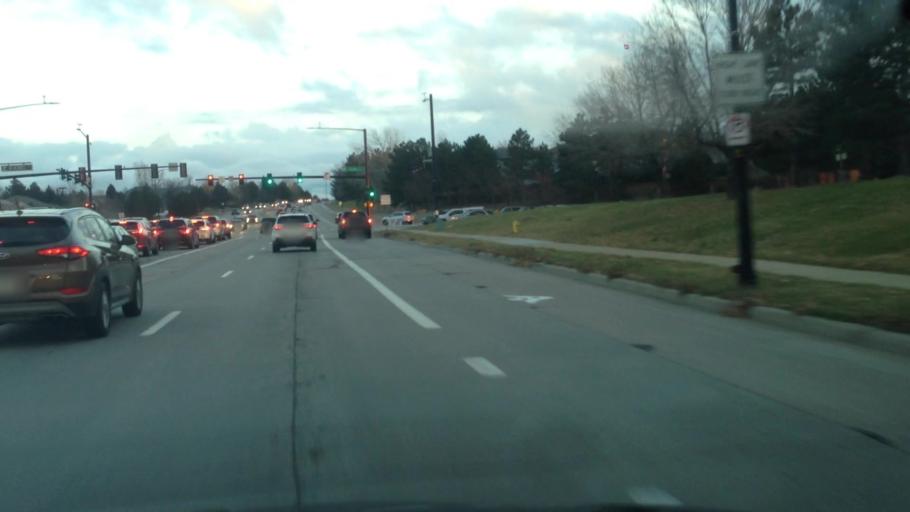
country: US
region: Colorado
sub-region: Douglas County
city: Carriage Club
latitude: 39.5425
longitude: -104.9144
